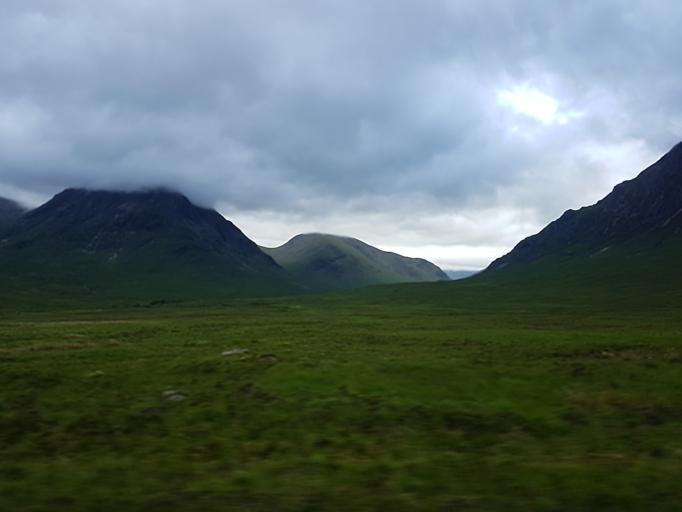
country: GB
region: Scotland
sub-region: Highland
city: Spean Bridge
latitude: 56.6548
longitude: -4.8645
